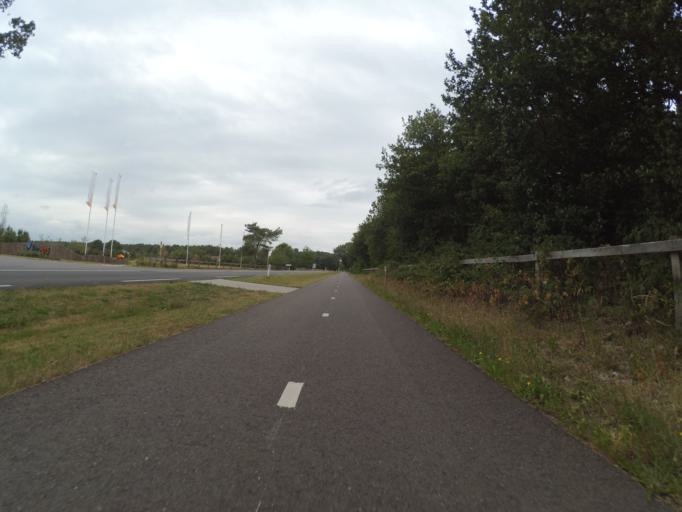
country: NL
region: Gelderland
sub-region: Gemeente Ede
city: Otterlo
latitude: 52.0873
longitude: 5.7767
